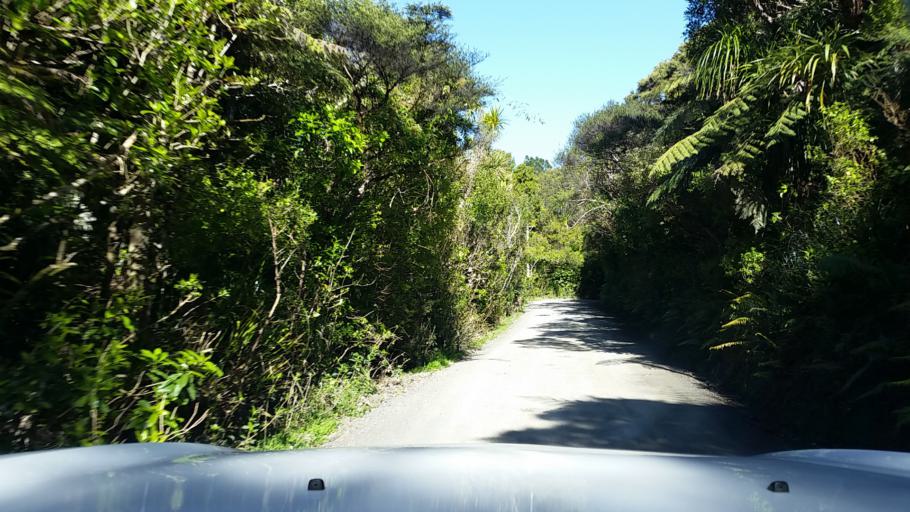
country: NZ
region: Auckland
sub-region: Auckland
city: Titirangi
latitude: -37.0233
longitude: 174.5349
